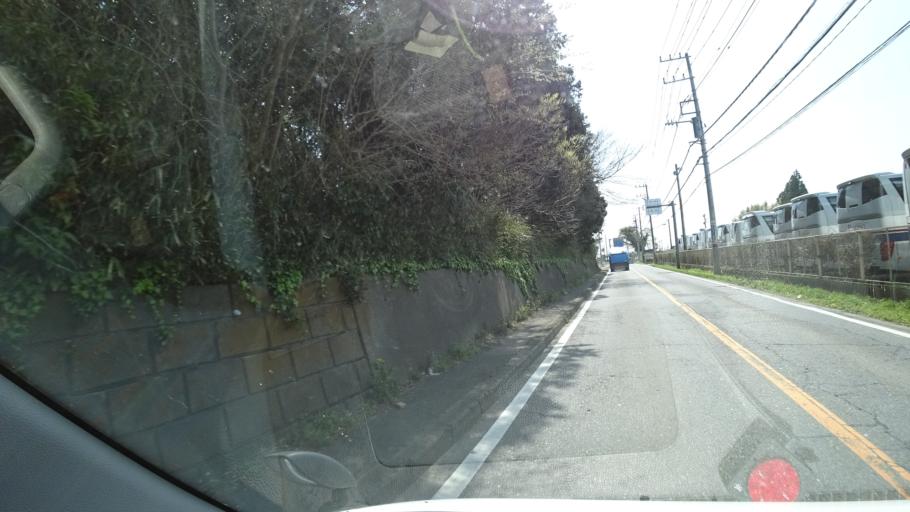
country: JP
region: Chiba
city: Narita
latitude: 35.7729
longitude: 140.3527
